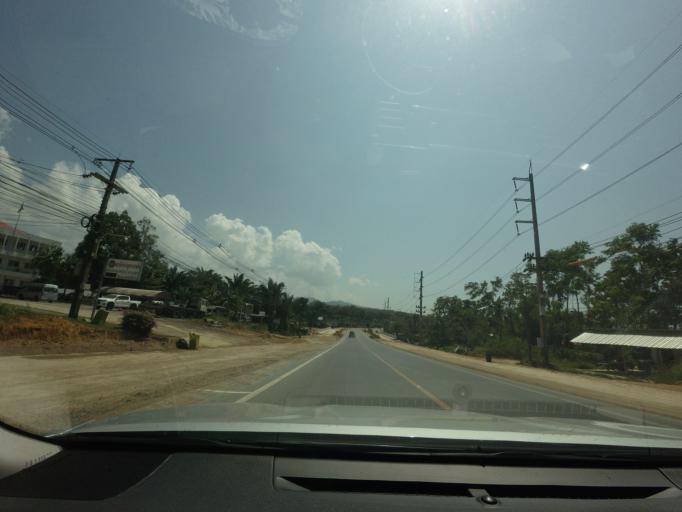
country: TH
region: Phangnga
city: Ban Khao Lak
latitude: 8.7035
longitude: 98.2583
